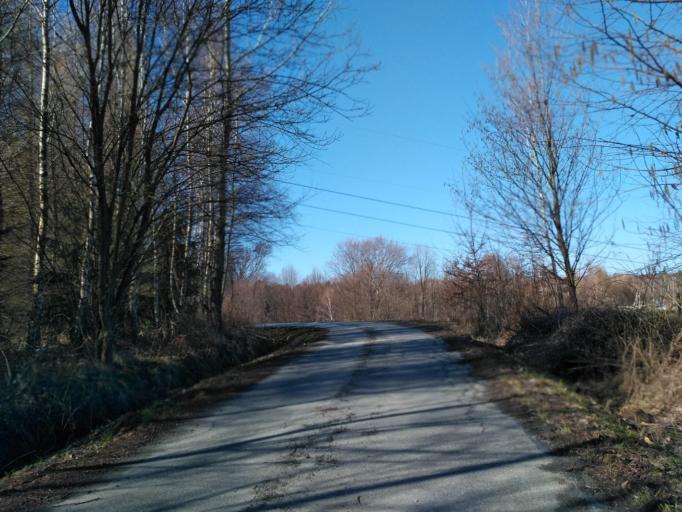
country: PL
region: Subcarpathian Voivodeship
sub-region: Powiat rzeszowski
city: Lutoryz
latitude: 49.9533
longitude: 21.8920
